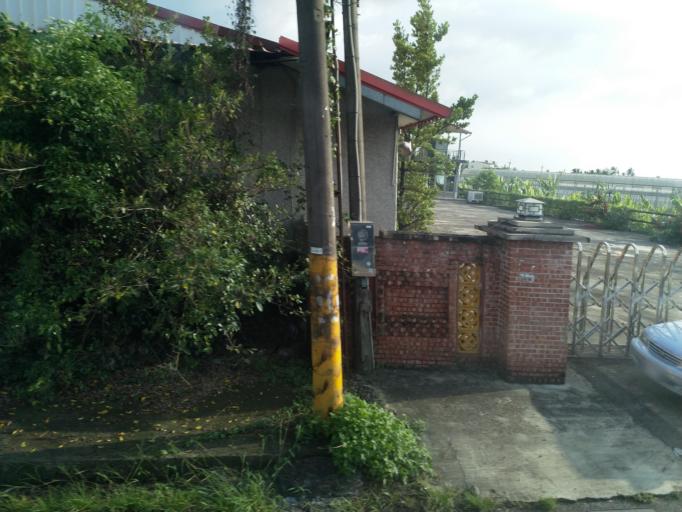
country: TW
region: Taiwan
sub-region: Pingtung
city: Pingtung
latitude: 22.8851
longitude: 120.5069
